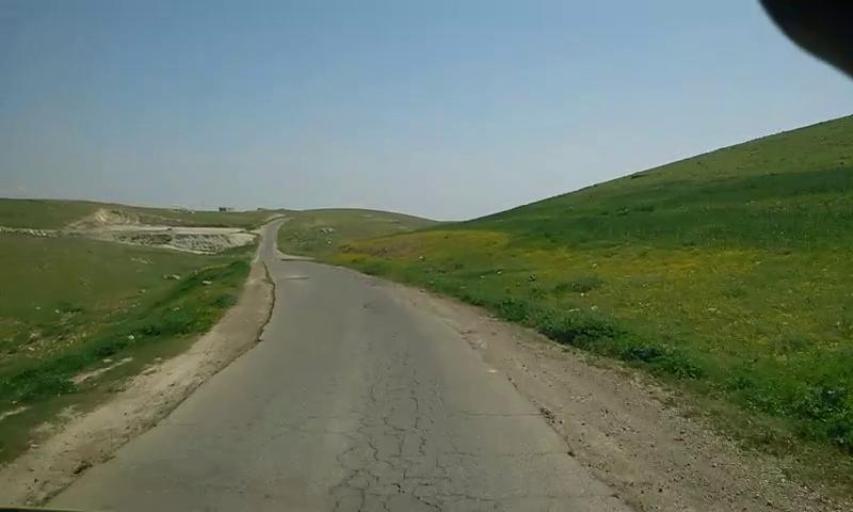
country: PS
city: `Arab ar Rashaydah
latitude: 31.5477
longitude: 35.2559
